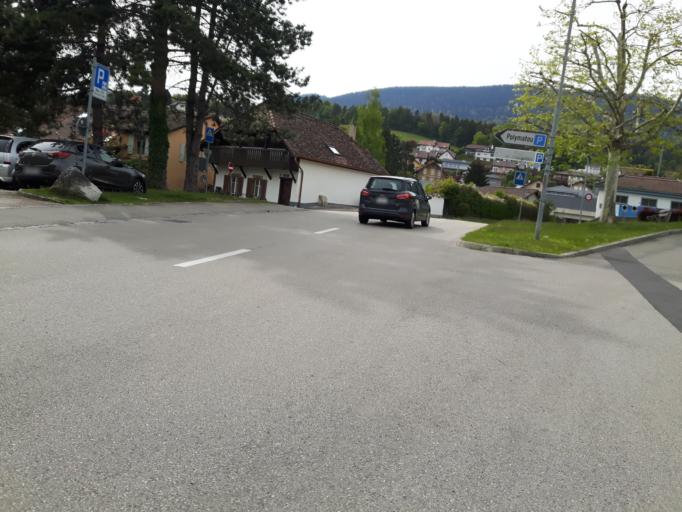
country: CH
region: Neuchatel
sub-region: Boudry District
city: Bevaix
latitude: 46.9313
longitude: 6.8141
